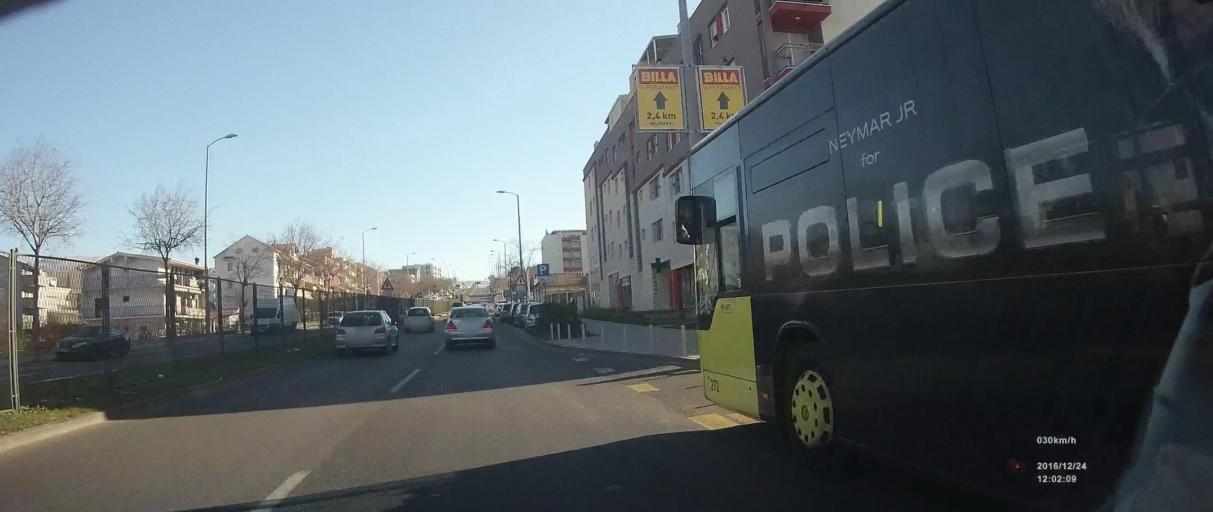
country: HR
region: Splitsko-Dalmatinska
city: Vranjic
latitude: 43.5164
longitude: 16.4872
